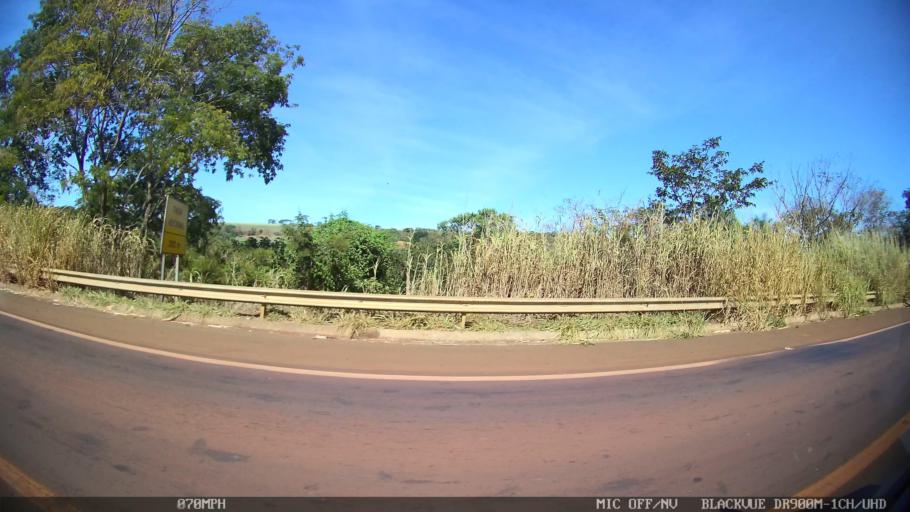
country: BR
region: Sao Paulo
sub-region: Sao Joaquim Da Barra
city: Sao Joaquim da Barra
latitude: -20.5532
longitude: -47.6650
